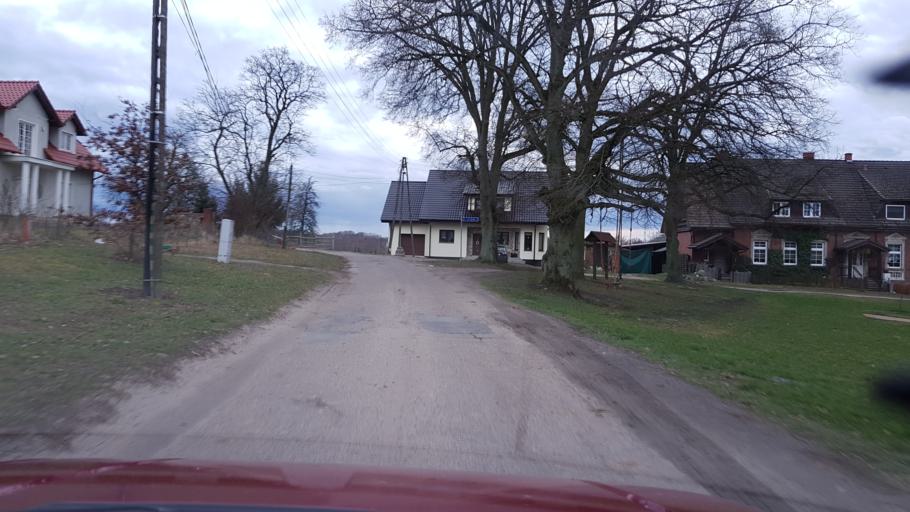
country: PL
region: West Pomeranian Voivodeship
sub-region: Powiat gryfinski
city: Stare Czarnowo
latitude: 53.3250
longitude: 14.6827
